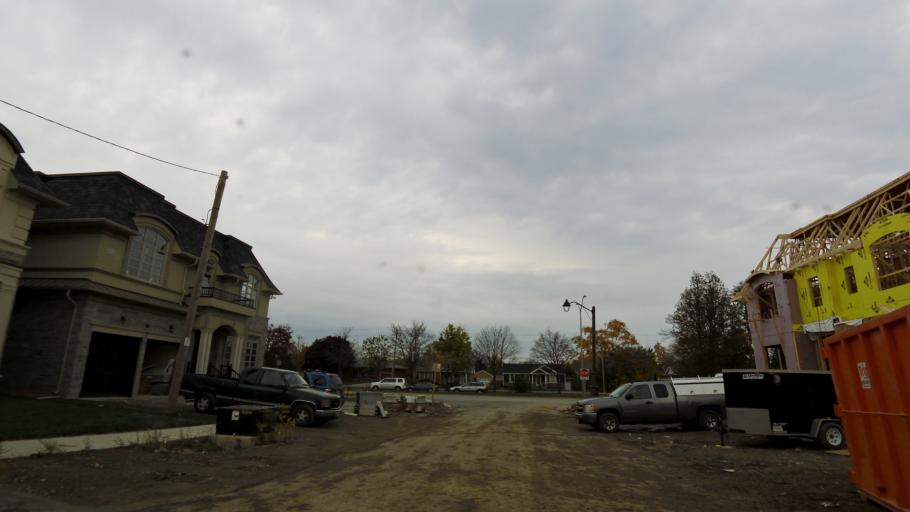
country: CA
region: Ontario
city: Oakville
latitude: 43.4386
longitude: -79.6852
